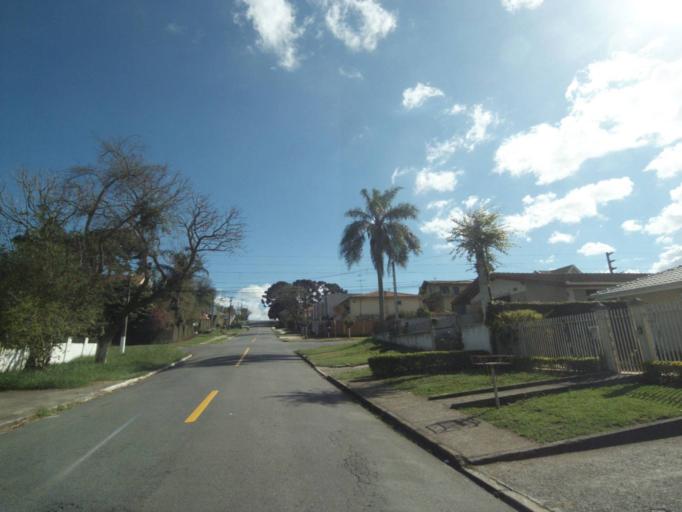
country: BR
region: Parana
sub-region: Curitiba
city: Curitiba
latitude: -25.3816
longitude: -49.2541
